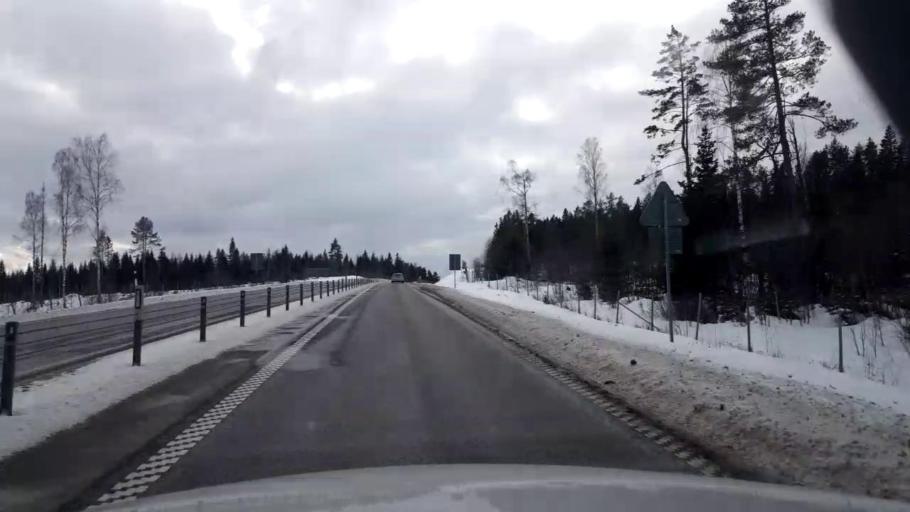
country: SE
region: Vaesternorrland
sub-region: Sundsvalls Kommun
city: Njurundabommen
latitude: 62.0938
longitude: 17.3048
